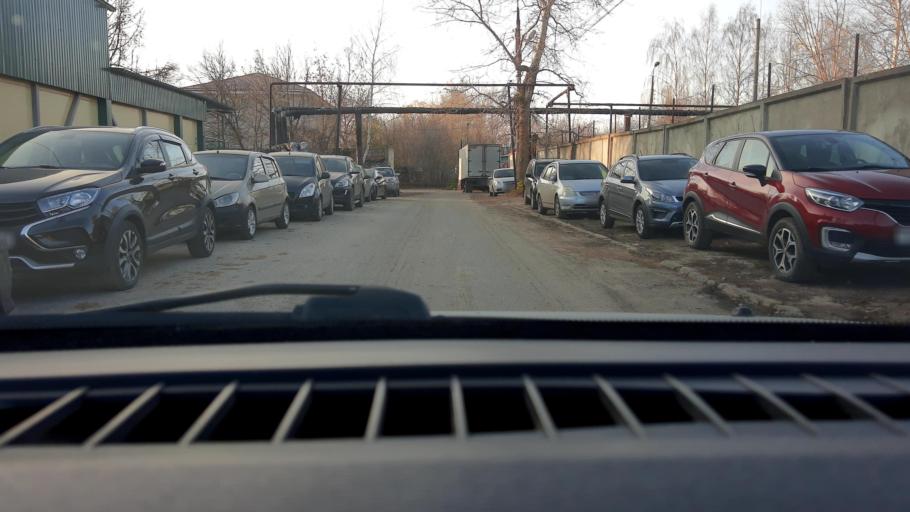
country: RU
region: Nizjnij Novgorod
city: Gorbatovka
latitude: 56.3193
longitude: 43.8592
